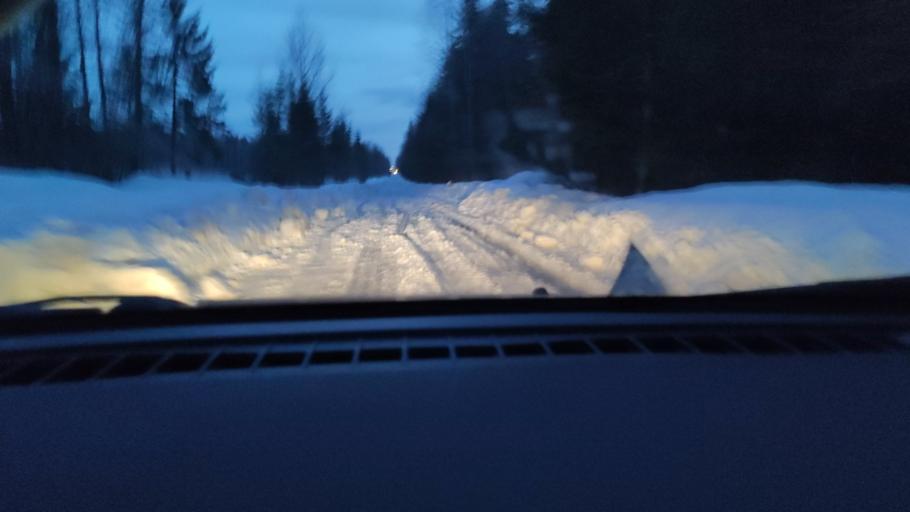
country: RU
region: Perm
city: Kondratovo
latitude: 58.0726
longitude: 56.1284
